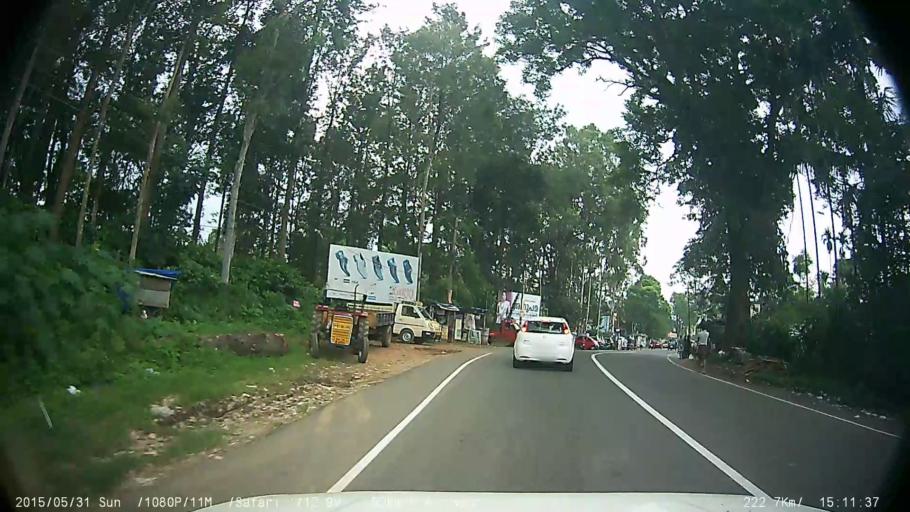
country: IN
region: Kerala
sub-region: Wayanad
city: Panamaram
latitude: 11.6617
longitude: 76.2331
